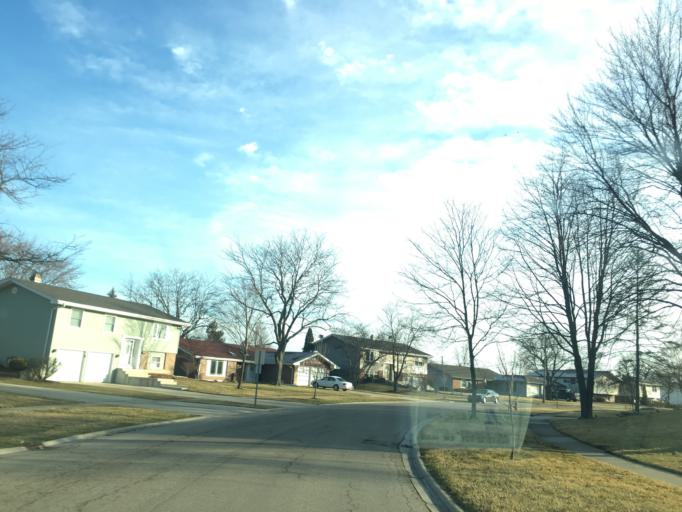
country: US
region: Illinois
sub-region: Cook County
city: South Barrington
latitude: 42.0564
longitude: -88.1135
